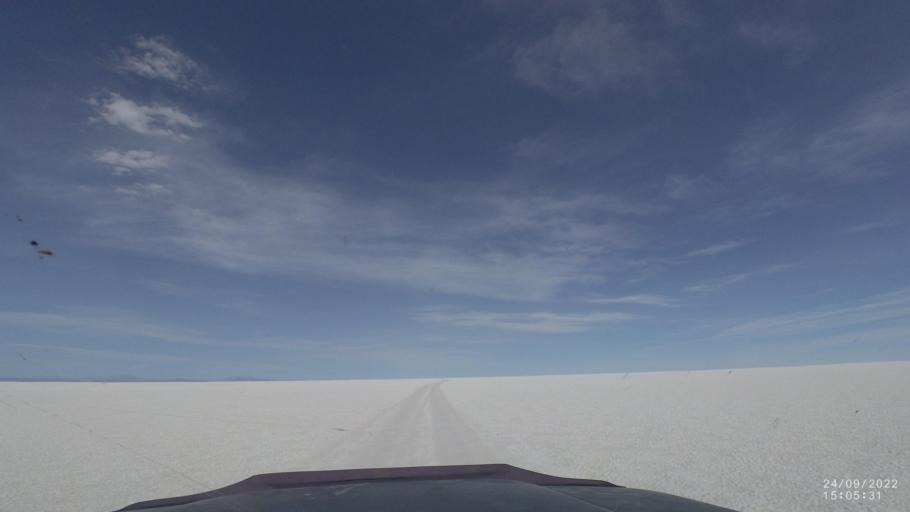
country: BO
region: Potosi
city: Colchani
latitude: -19.9068
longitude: -67.5166
